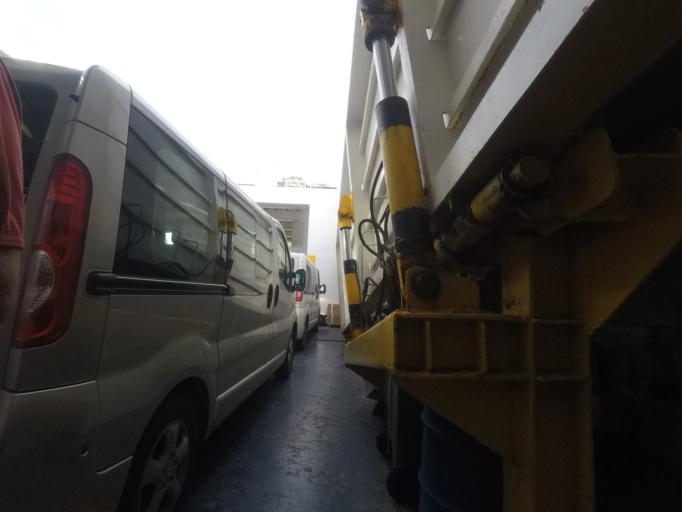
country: HR
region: Splitsko-Dalmatinska
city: Stari Grad
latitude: 43.1816
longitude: 16.5761
